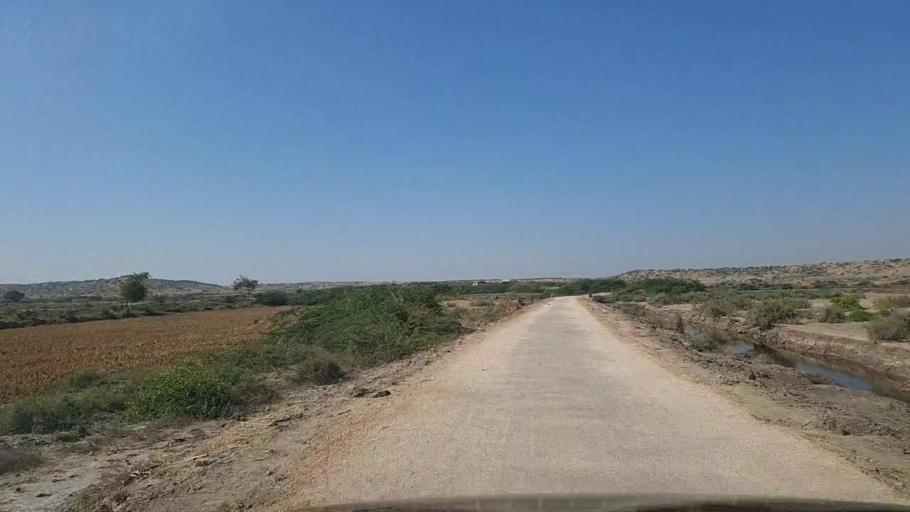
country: PK
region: Sindh
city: Thatta
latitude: 24.6299
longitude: 67.8691
